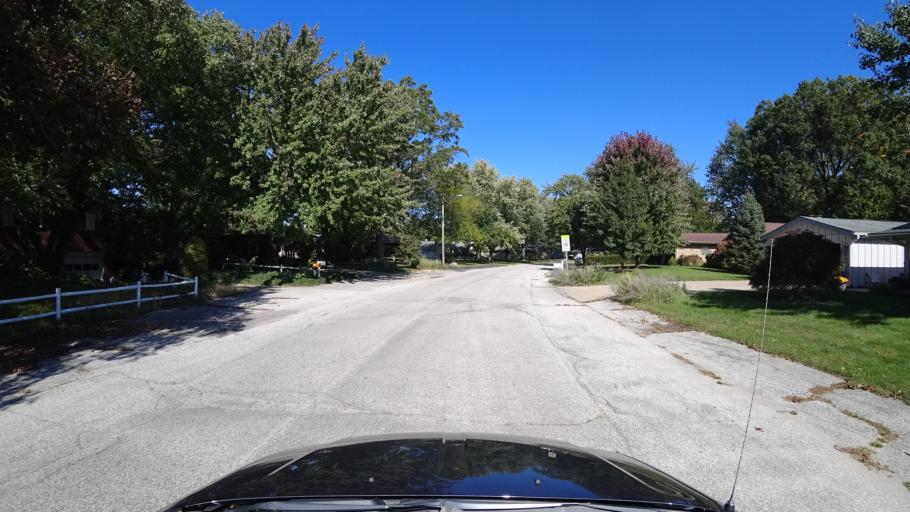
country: US
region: Indiana
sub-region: LaPorte County
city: Michigan City
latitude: 41.6899
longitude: -86.8911
